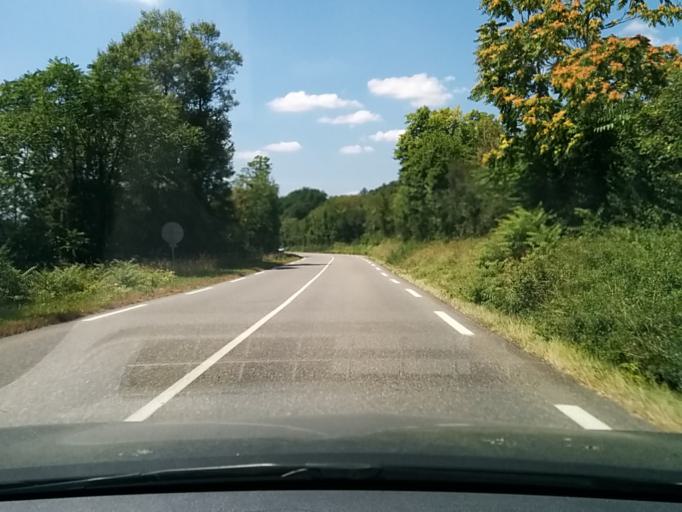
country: FR
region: Midi-Pyrenees
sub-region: Departement du Gers
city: Vic-Fezensac
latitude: 43.7491
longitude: 0.3341
